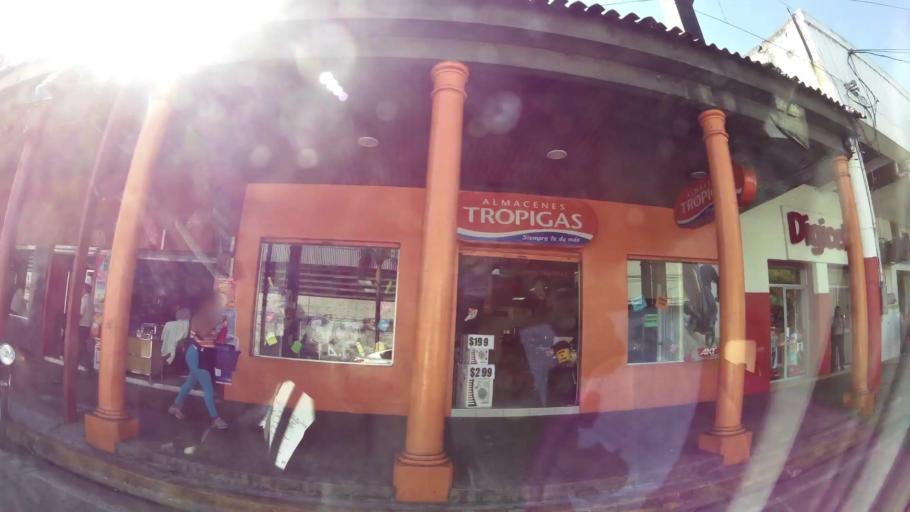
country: SV
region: La Libertad
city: Santa Tecla
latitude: 13.6731
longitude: -89.2878
